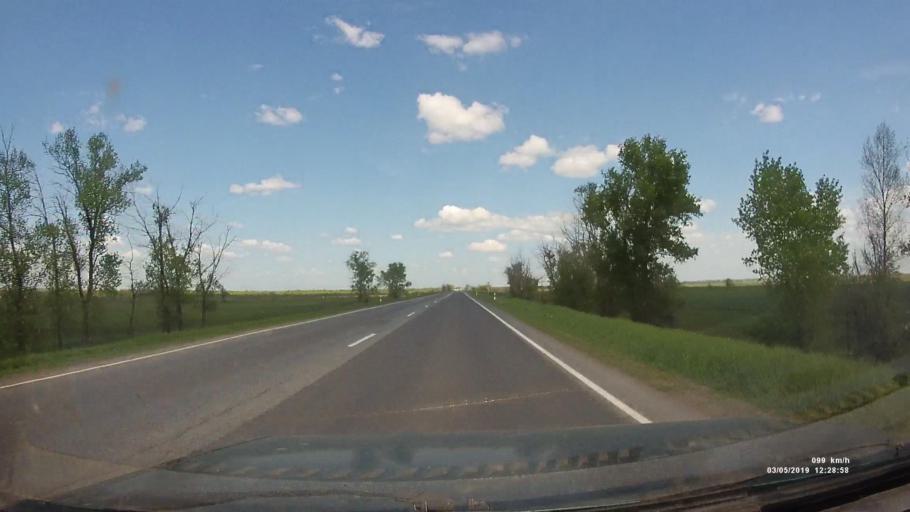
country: RU
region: Rostov
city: Semikarakorsk
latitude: 47.4809
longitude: 40.7322
